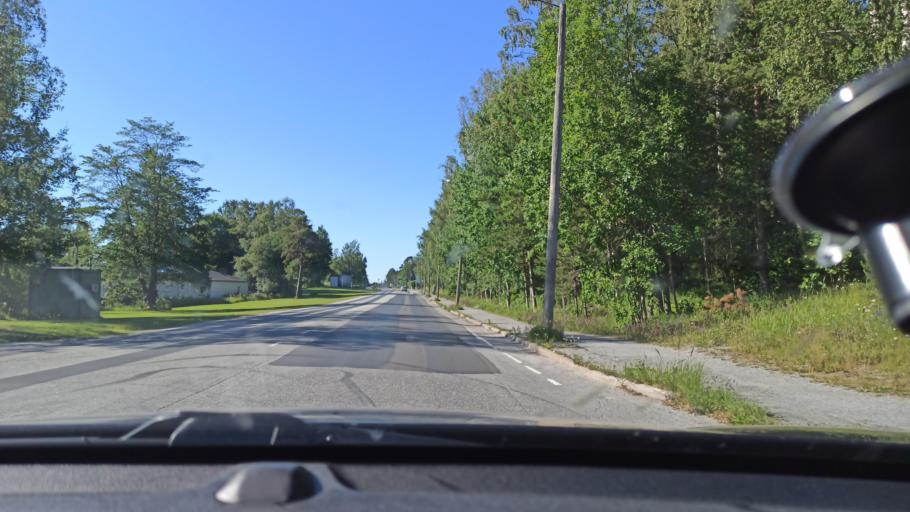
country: FI
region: Ostrobothnia
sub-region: Jakobstadsregionen
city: Jakobstad
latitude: 63.6788
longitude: 22.7191
